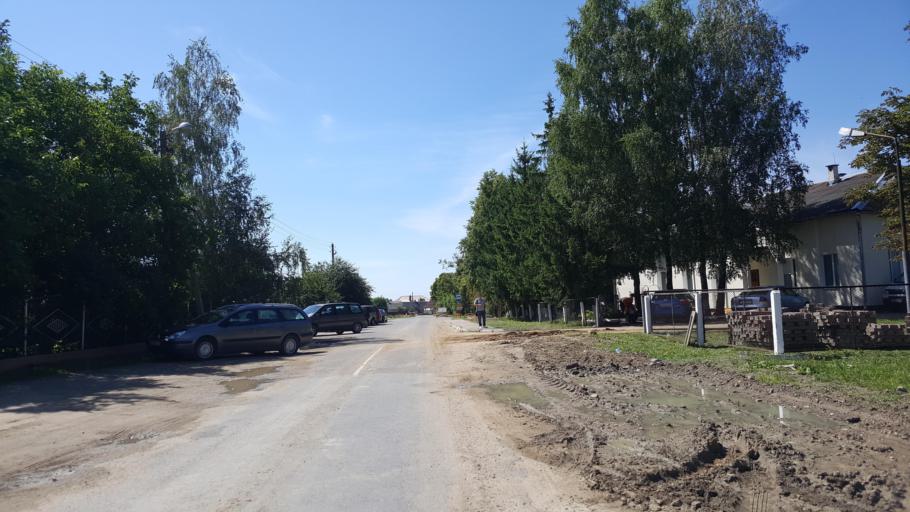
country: BY
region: Brest
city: Charnawchytsy
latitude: 52.2267
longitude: 23.7396
